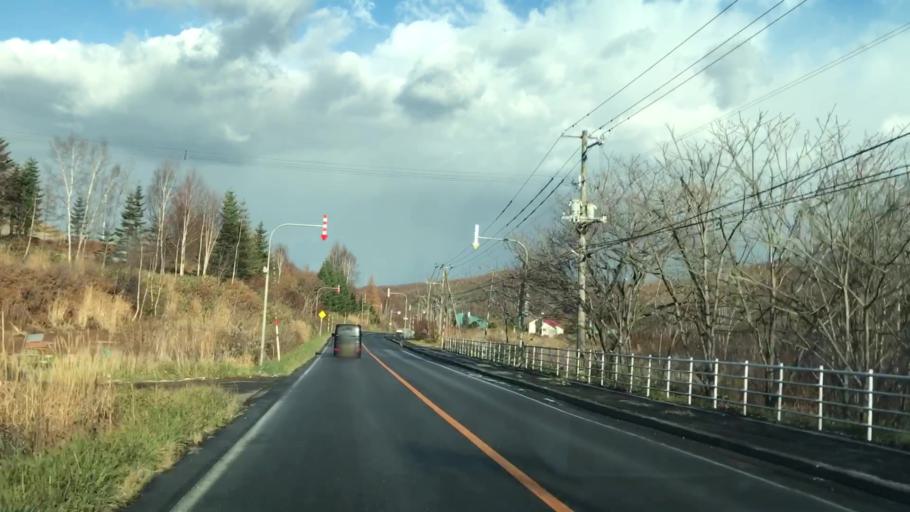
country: JP
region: Hokkaido
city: Otaru
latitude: 43.1884
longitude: 140.9598
